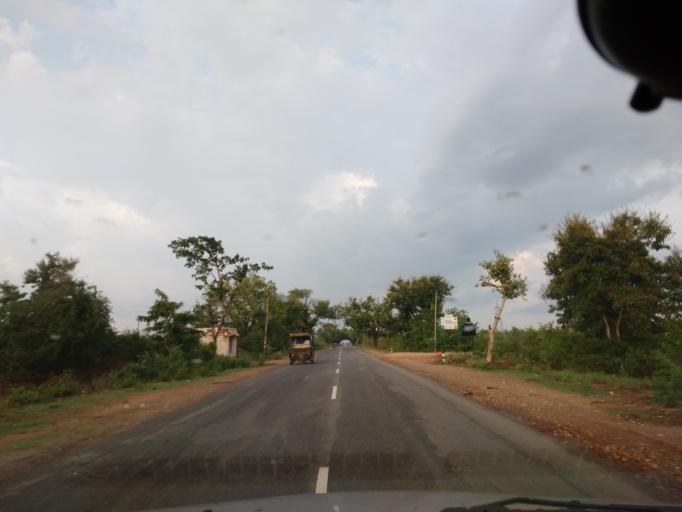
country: IN
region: Karnataka
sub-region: Tumkur
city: Tiptur
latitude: 13.2676
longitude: 76.4060
